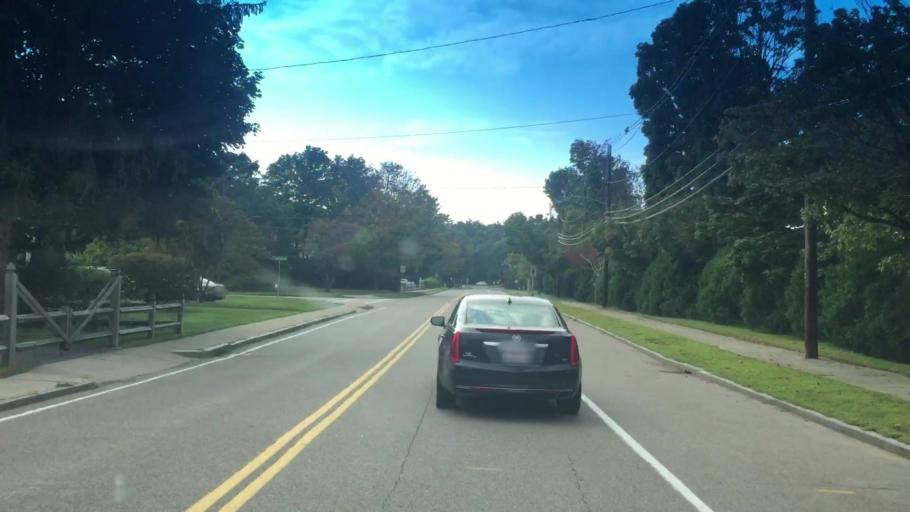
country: US
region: Massachusetts
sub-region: Norfolk County
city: Westwood
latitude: 42.2064
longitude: -71.2333
